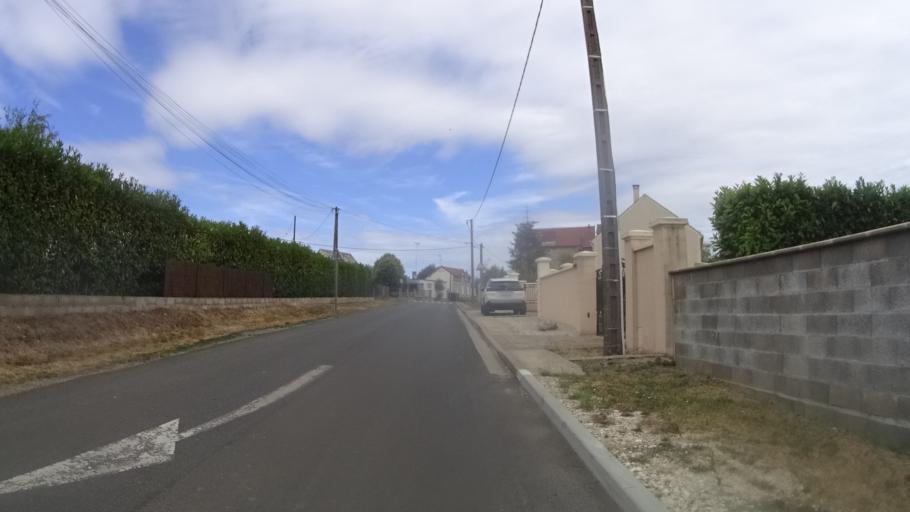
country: FR
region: Centre
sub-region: Departement du Loiret
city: Malesherbes
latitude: 48.2249
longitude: 2.4234
